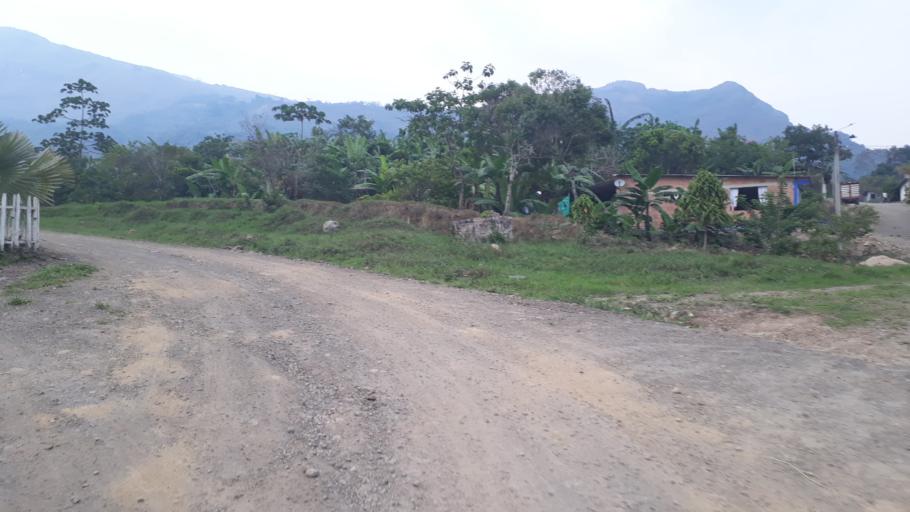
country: CO
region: Casanare
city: Nunchia
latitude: 5.6240
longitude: -72.4254
